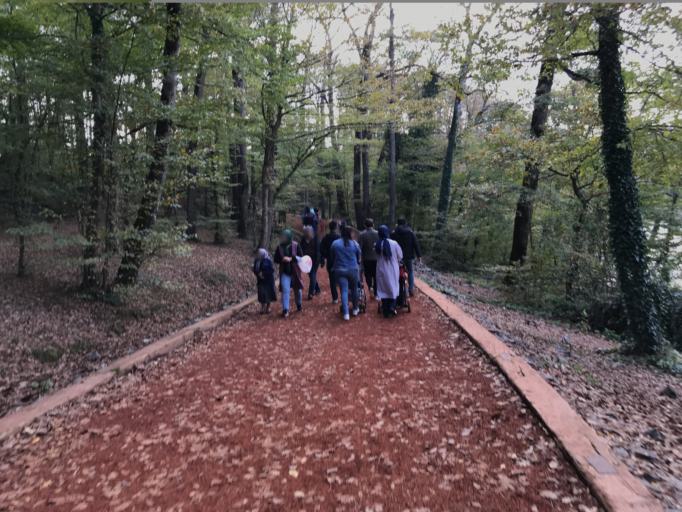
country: TR
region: Istanbul
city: Kemerburgaz
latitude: 41.1752
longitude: 28.9587
